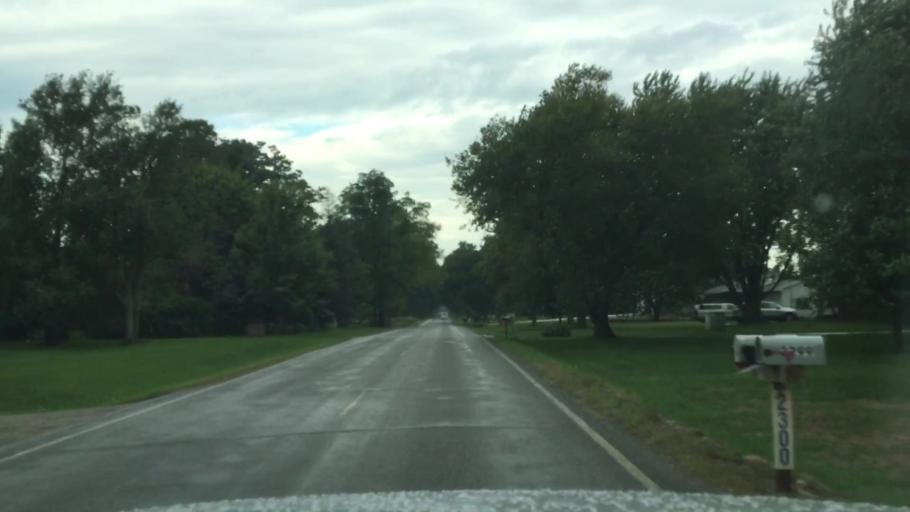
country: US
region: Michigan
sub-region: Shiawassee County
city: Perry
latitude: 42.8927
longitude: -84.2081
